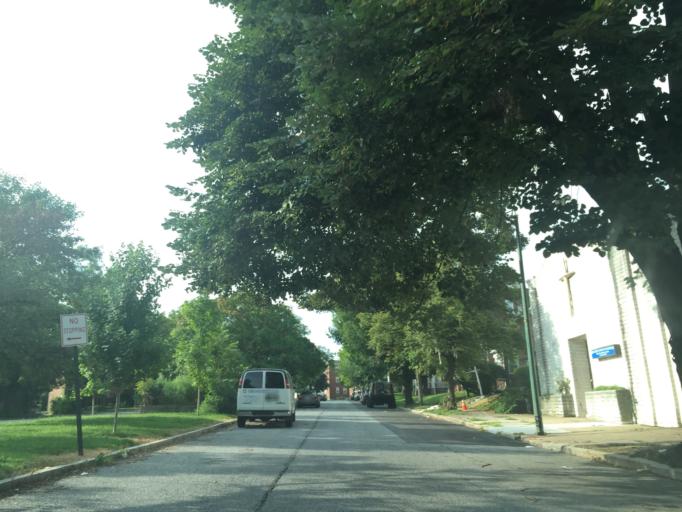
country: US
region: Maryland
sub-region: City of Baltimore
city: Baltimore
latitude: 39.3165
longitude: -76.6304
